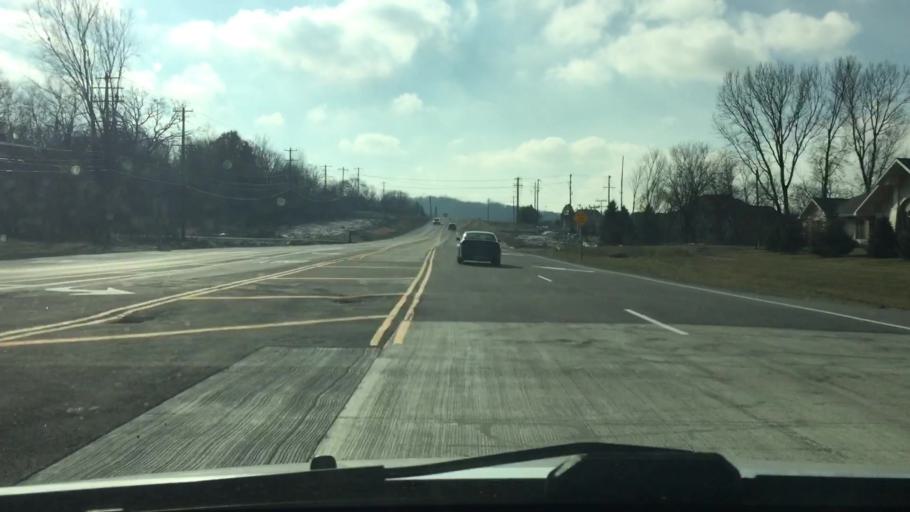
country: US
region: Wisconsin
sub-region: Waukesha County
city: Waukesha
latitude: 43.0183
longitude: -88.2860
